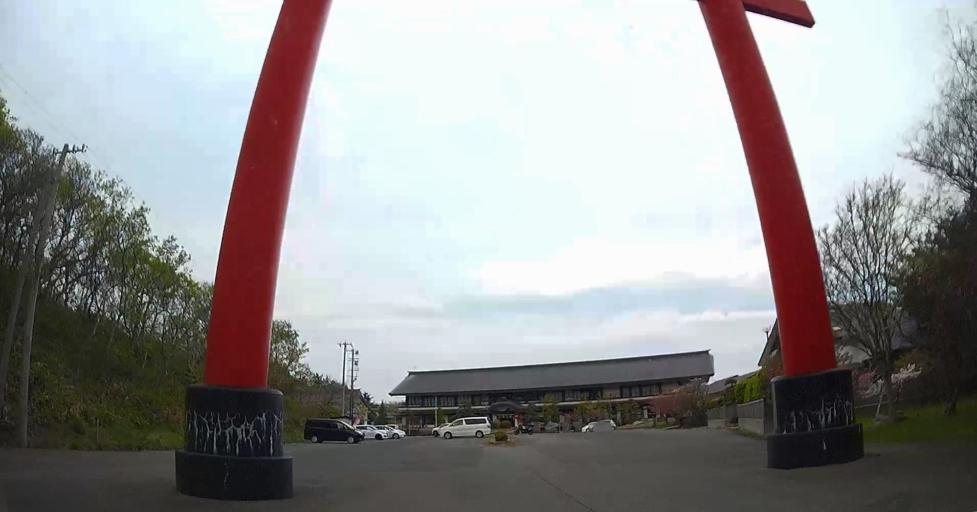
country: JP
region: Aomori
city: Shimokizukuri
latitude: 40.9384
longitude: 140.3137
